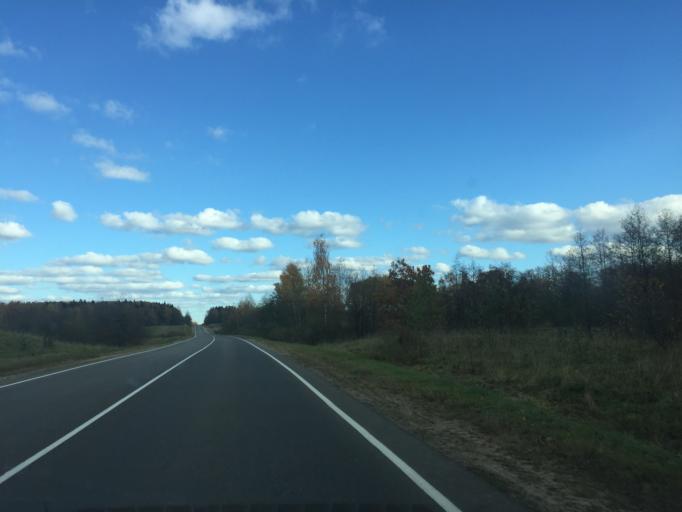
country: BY
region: Minsk
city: Narach
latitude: 54.9958
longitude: 26.7874
